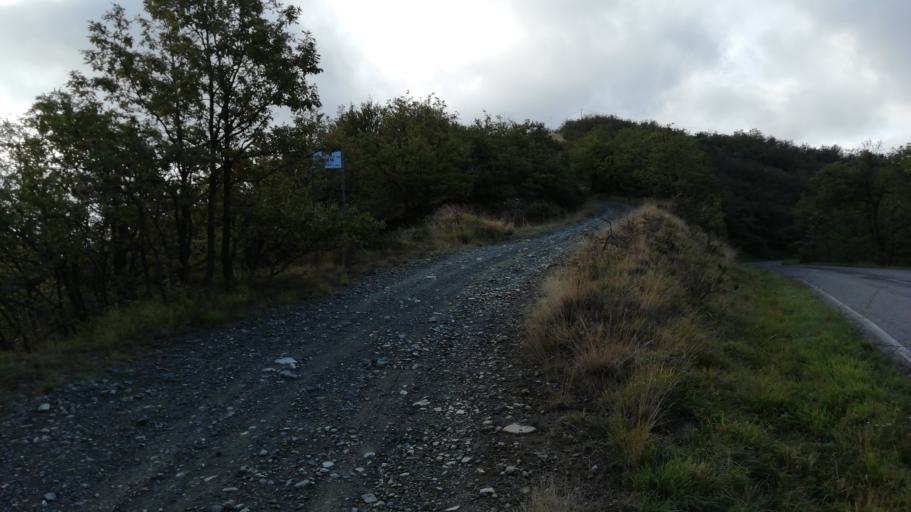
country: IT
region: Piedmont
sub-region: Provincia di Alessandria
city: Bosio
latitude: 44.6219
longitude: 8.7905
